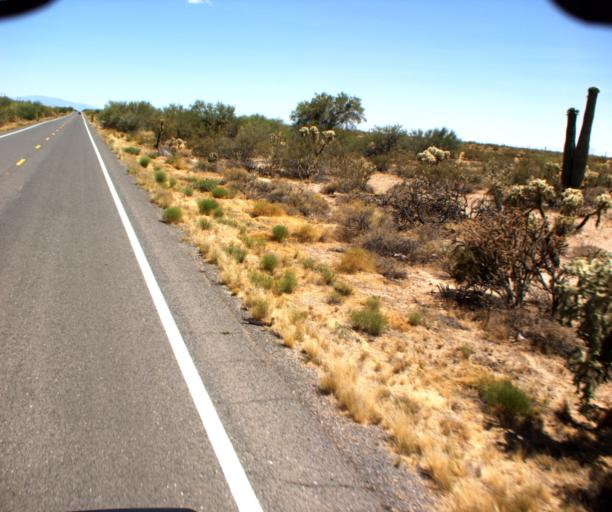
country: US
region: Arizona
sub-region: Pinal County
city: Florence
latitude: 32.8768
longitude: -111.2559
